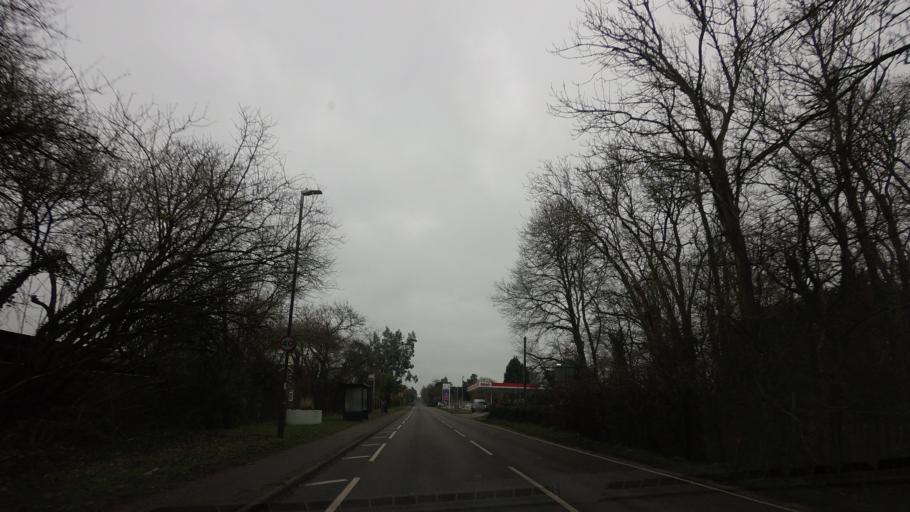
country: GB
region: England
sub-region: Kent
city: Staplehurst
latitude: 51.1543
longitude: 0.5523
